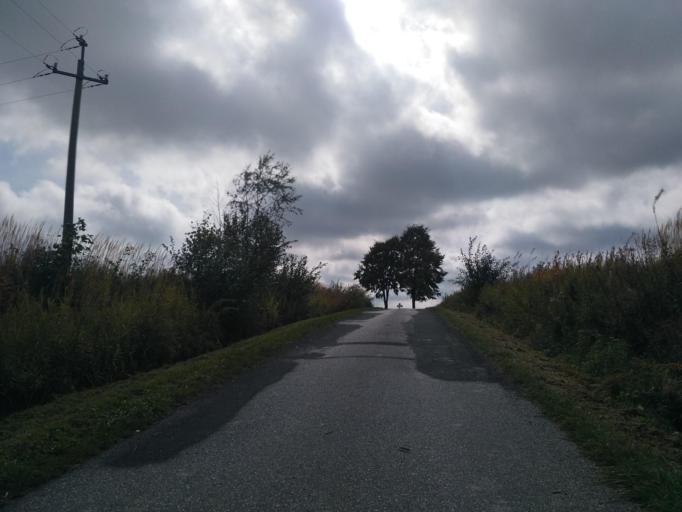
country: PL
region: Subcarpathian Voivodeship
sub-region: Powiat ropczycko-sedziszowski
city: Niedzwiada
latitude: 49.9219
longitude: 21.4848
